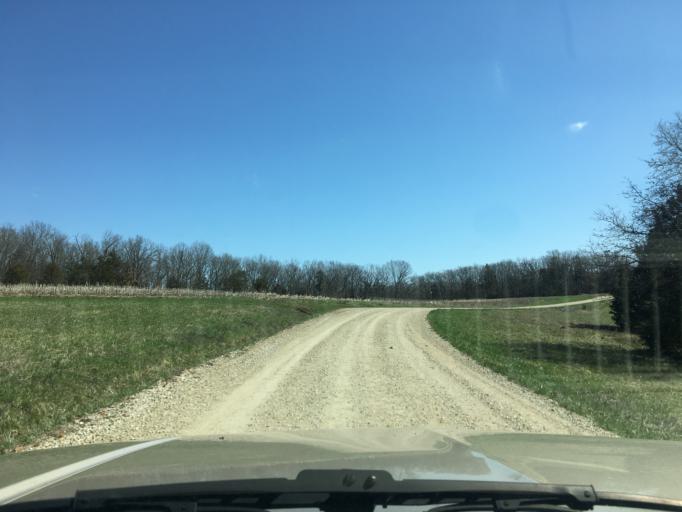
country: US
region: Missouri
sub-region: Franklin County
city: New Haven
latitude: 38.5530
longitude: -91.3197
